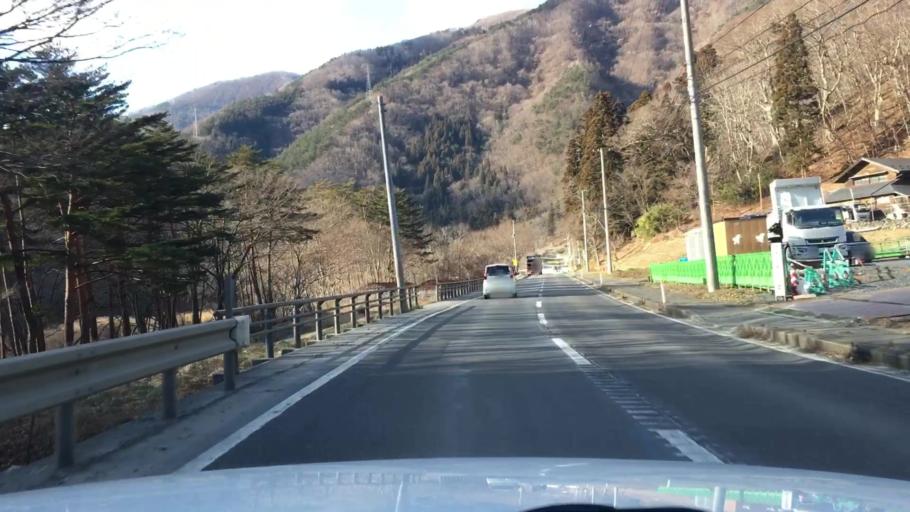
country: JP
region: Iwate
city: Miyako
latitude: 39.6019
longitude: 141.7019
